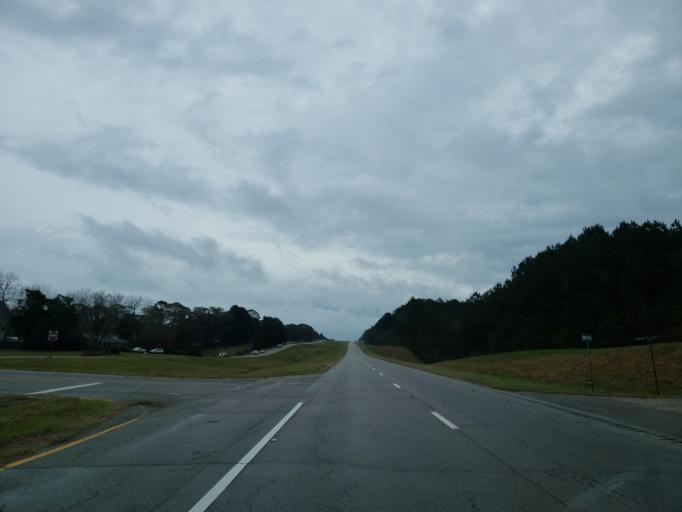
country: US
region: Mississippi
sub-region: Jones County
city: Sharon
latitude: 31.6967
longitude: -88.8851
